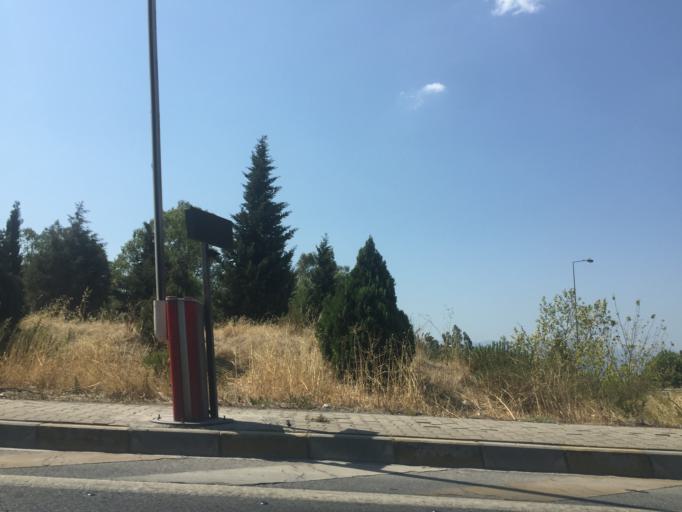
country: TR
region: Izmir
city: Karsiyaka
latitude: 38.4826
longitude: 27.1465
